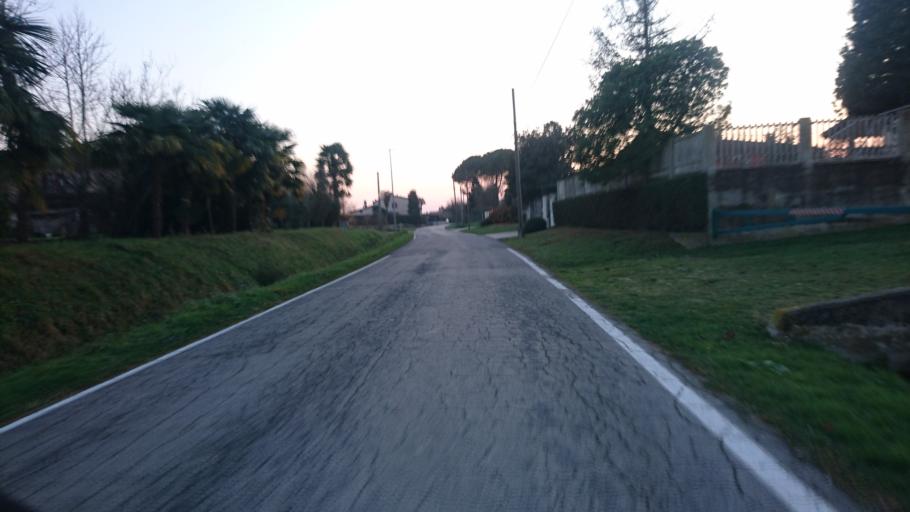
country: IT
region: Veneto
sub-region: Provincia di Padova
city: Legnaro
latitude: 45.3596
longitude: 11.9644
